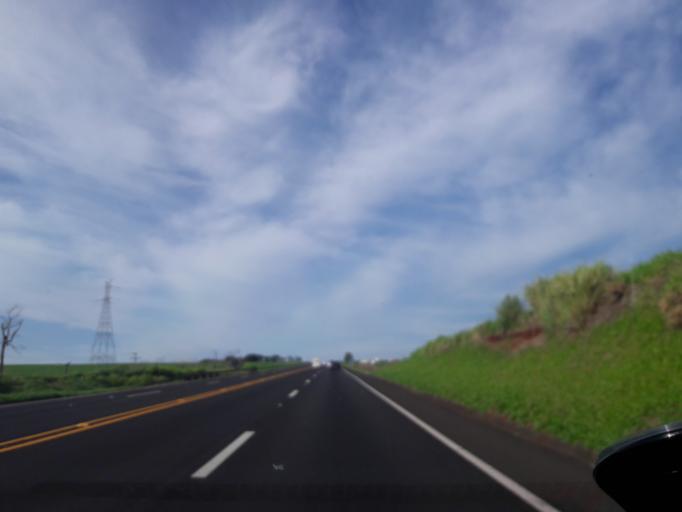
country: BR
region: Parana
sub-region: Apucarana
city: Apucarana
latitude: -23.4549
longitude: -51.5605
